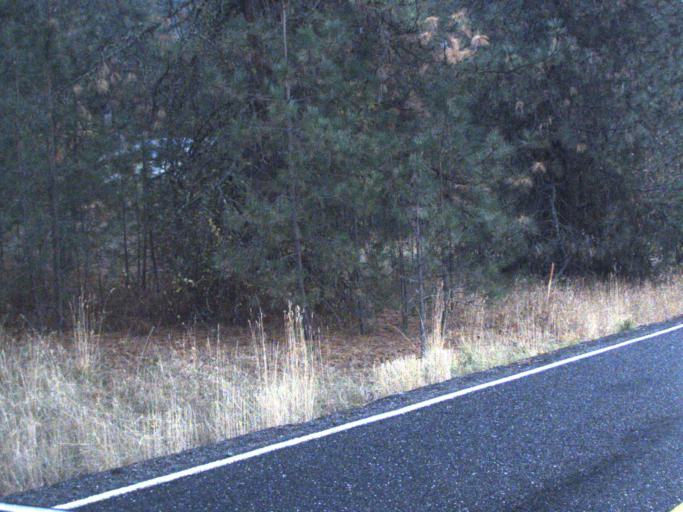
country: US
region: Washington
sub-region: Stevens County
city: Kettle Falls
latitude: 48.2491
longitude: -118.1371
